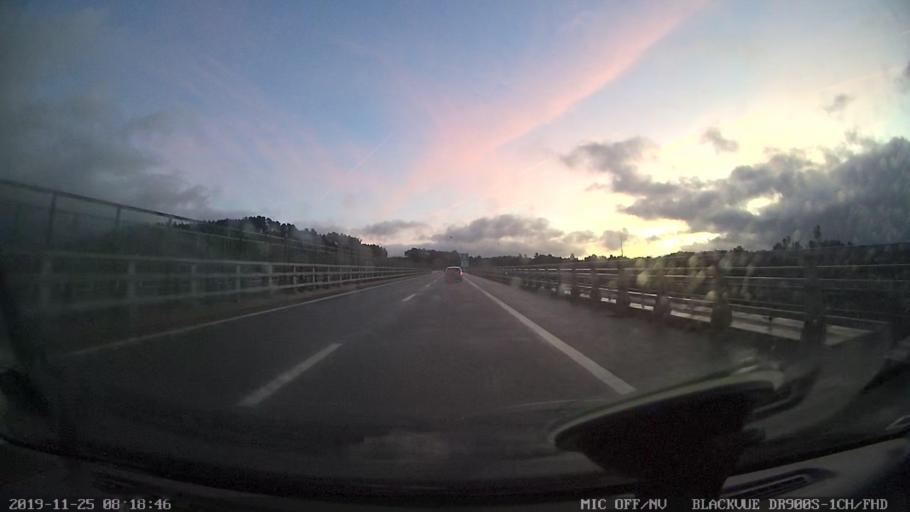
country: PT
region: Vila Real
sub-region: Vila Real
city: Vila Real
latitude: 41.2857
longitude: -7.7006
